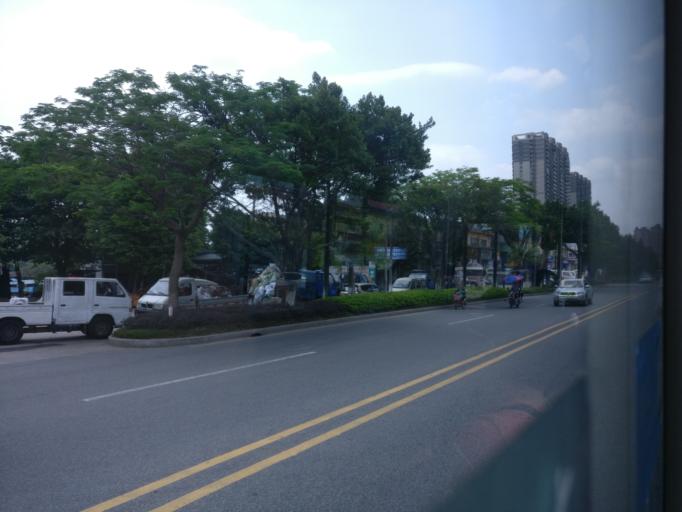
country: CN
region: Guangdong
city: Xiaoguwei
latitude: 23.0367
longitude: 113.3355
